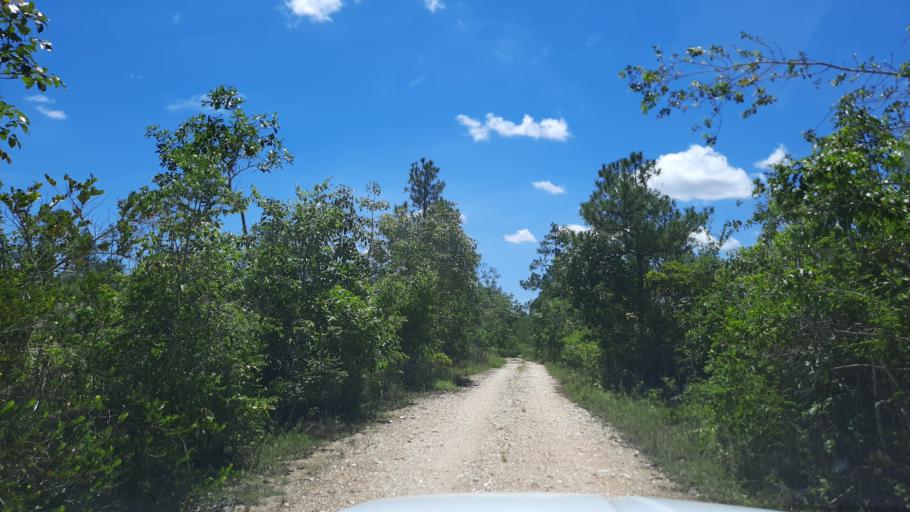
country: BZ
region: Cayo
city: Belmopan
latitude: 17.3556
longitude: -88.5451
